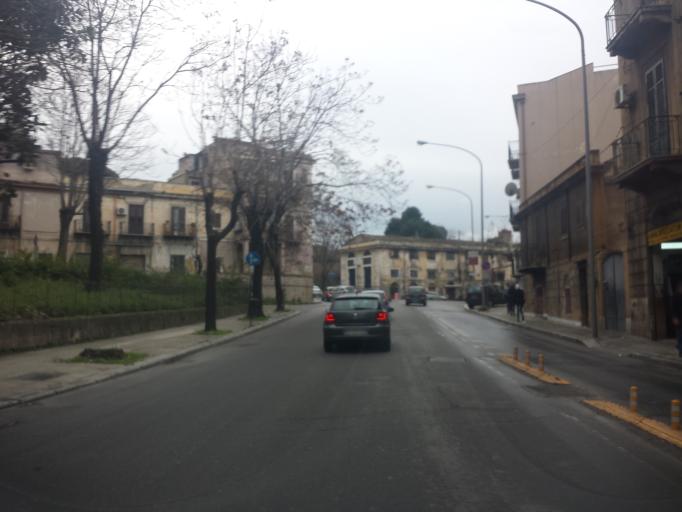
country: IT
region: Sicily
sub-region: Palermo
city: Palermo
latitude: 38.1127
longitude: 13.3521
